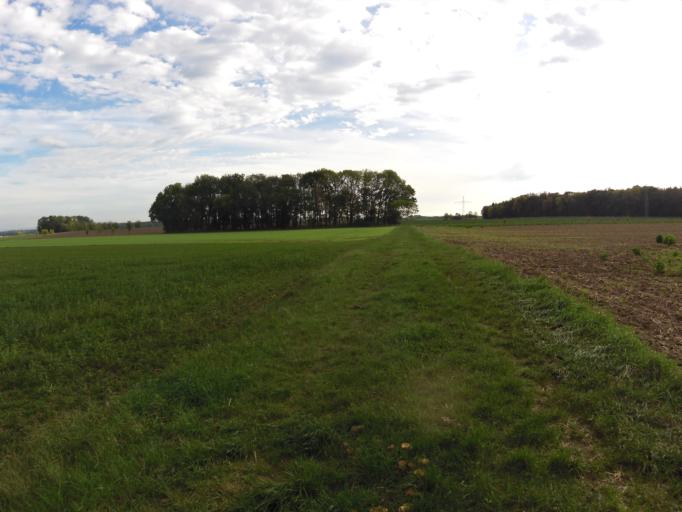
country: DE
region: Bavaria
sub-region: Regierungsbezirk Unterfranken
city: Biebelried
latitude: 49.7339
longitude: 10.0690
